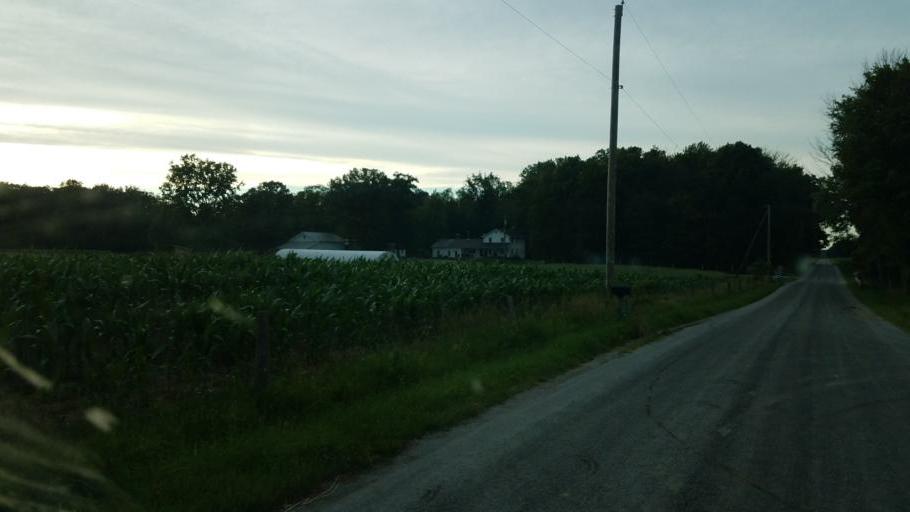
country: US
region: Ohio
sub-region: Huron County
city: Greenwich
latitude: 40.9253
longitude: -82.4748
